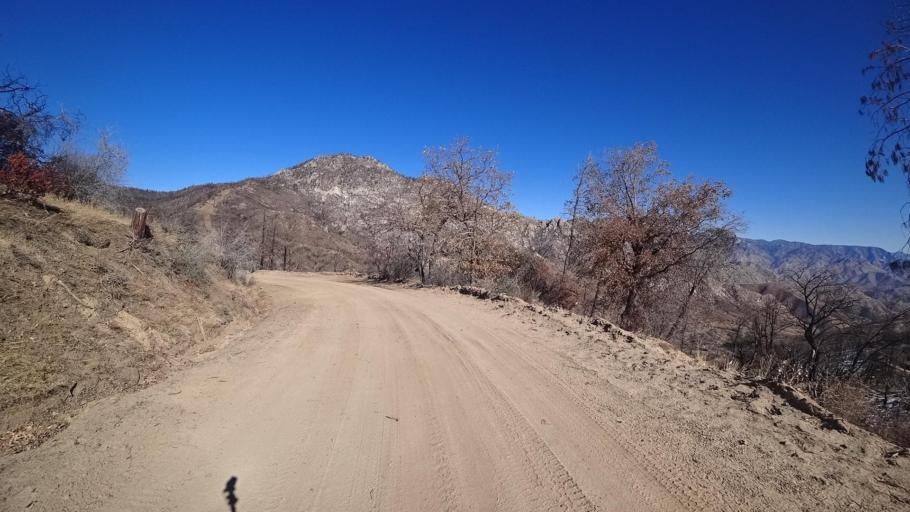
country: US
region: California
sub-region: Kern County
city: Alta Sierra
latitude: 35.7164
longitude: -118.5286
